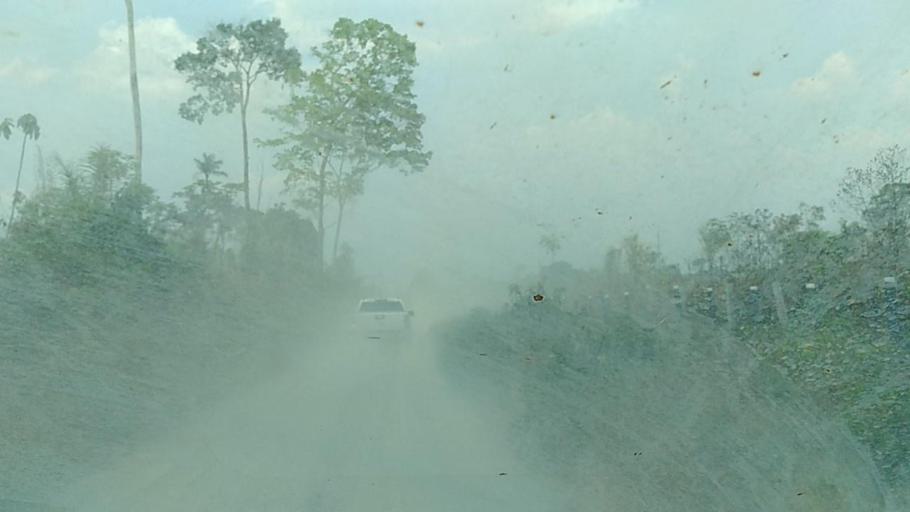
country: BR
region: Rondonia
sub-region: Porto Velho
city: Porto Velho
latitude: -8.7729
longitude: -63.2086
